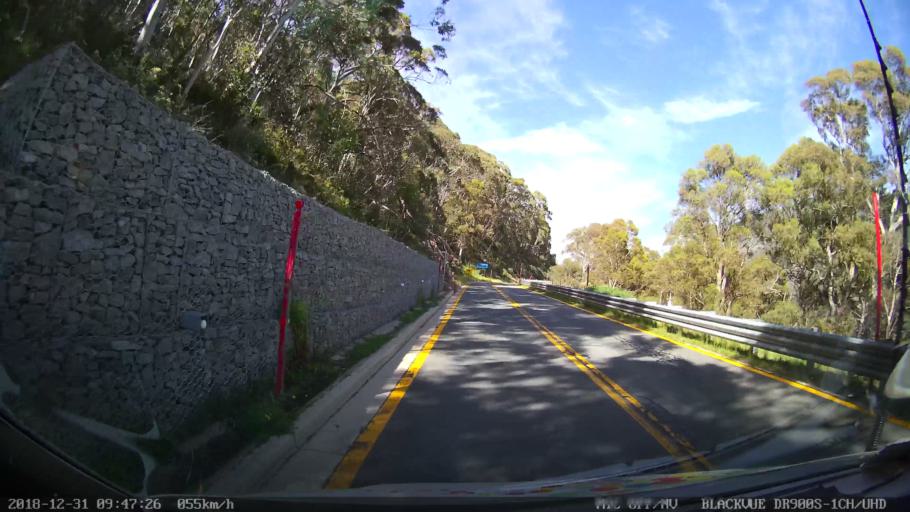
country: AU
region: New South Wales
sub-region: Snowy River
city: Jindabyne
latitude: -36.5084
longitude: 148.3017
